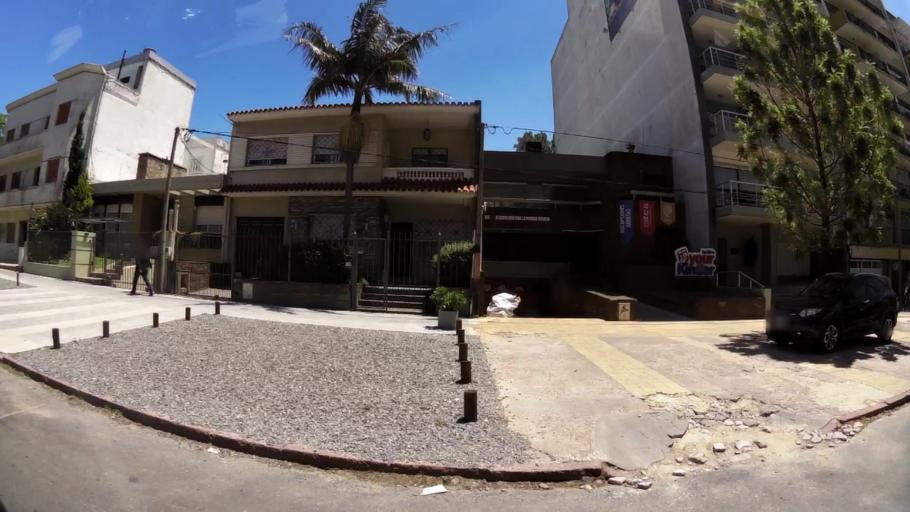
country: UY
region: Montevideo
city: Montevideo
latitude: -34.9012
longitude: -56.1603
